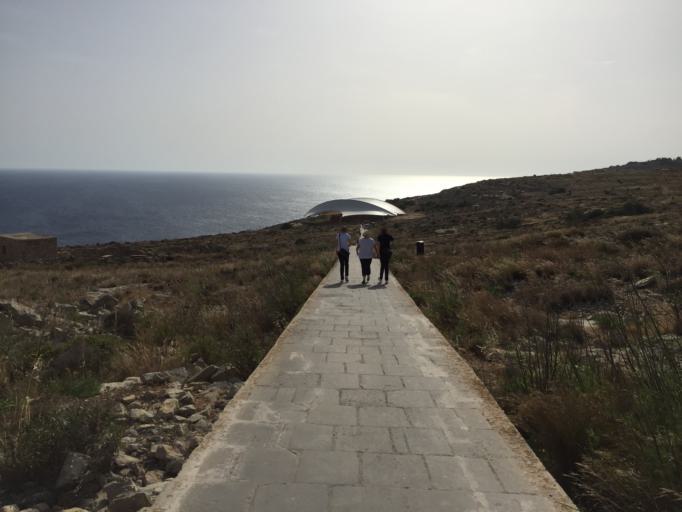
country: MT
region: Il-Qrendi
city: Qrendi
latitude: 35.8272
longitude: 14.4395
